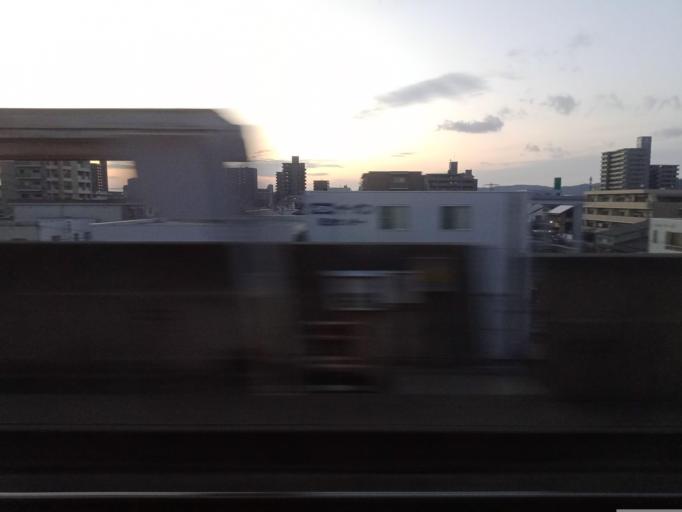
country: JP
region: Okayama
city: Okayama-shi
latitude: 34.6549
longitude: 133.9101
